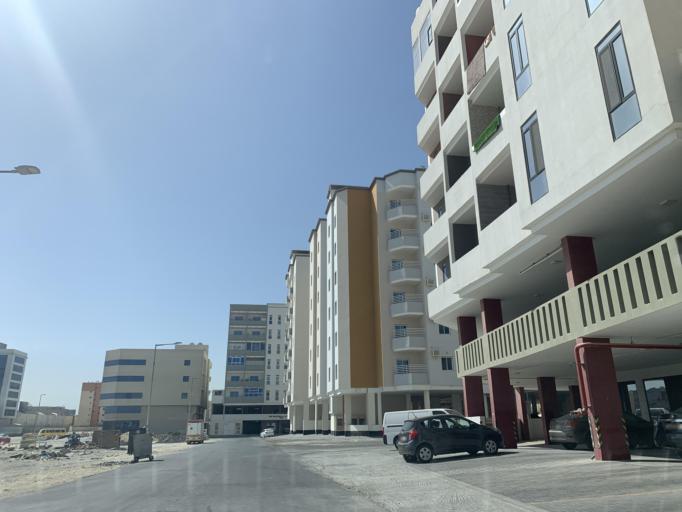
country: BH
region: Northern
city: Ar Rifa'
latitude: 26.1393
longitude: 50.5802
